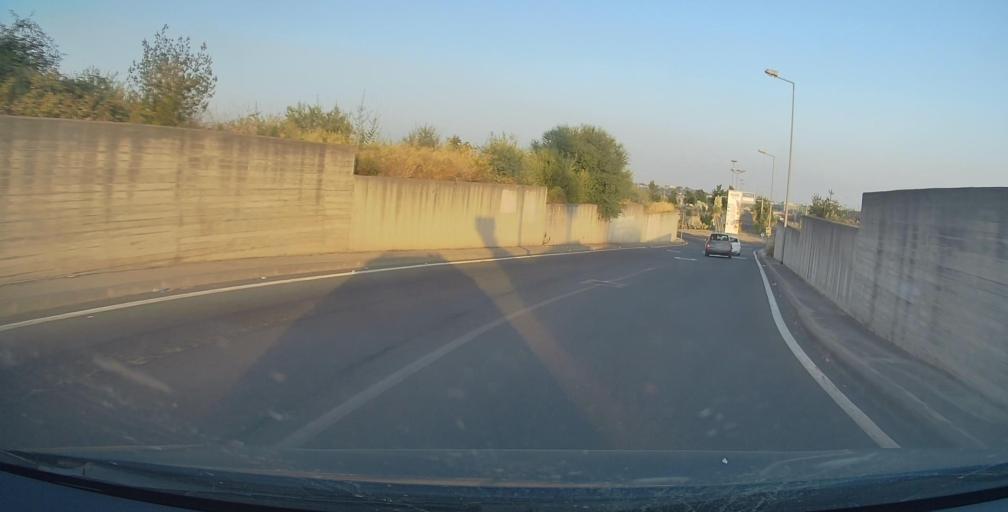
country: IT
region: Sicily
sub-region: Catania
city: Palazzolo
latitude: 37.5493
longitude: 14.9474
